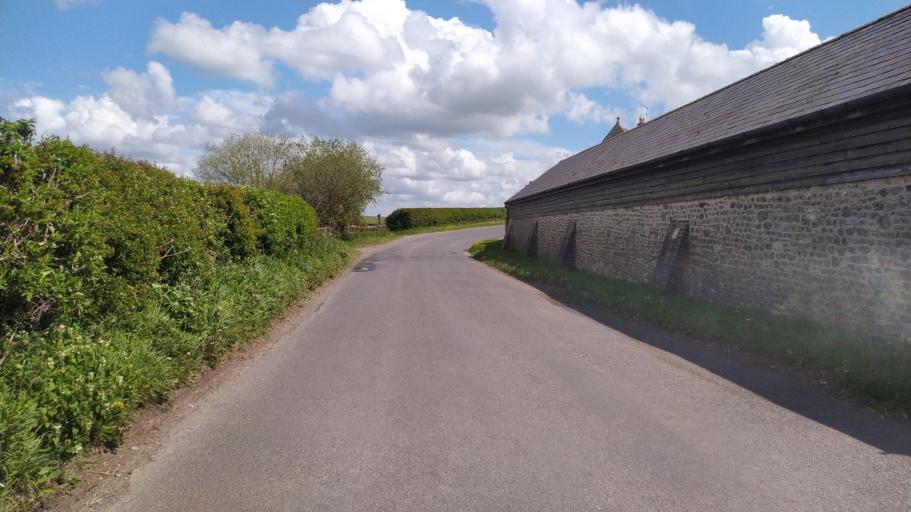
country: GB
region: England
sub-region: Wiltshire
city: Kilmington
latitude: 51.1568
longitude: -2.2696
